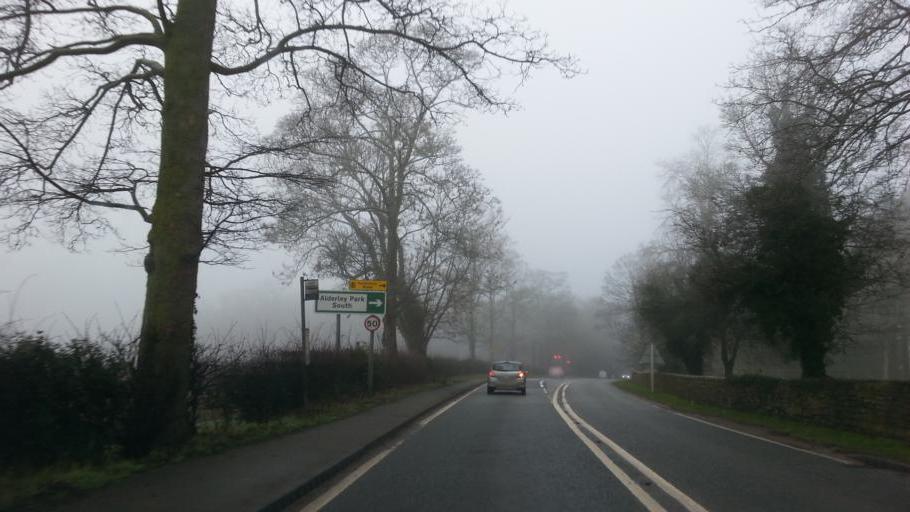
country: GB
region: England
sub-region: Cheshire East
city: Siddington
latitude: 53.2685
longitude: -2.2368
